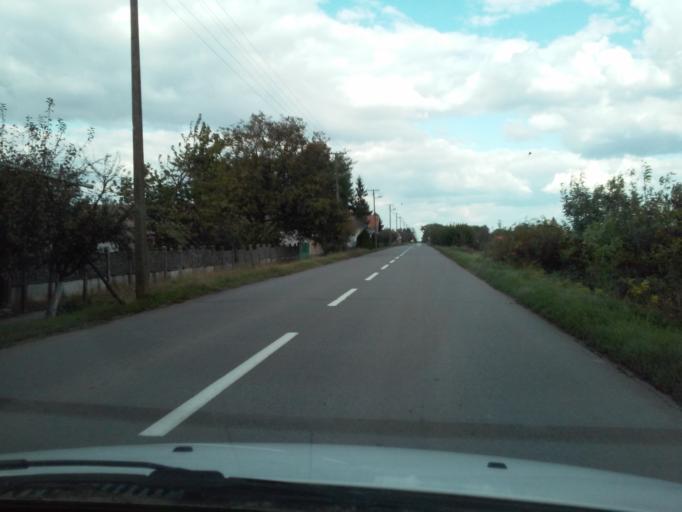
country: RS
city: Sajan
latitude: 45.8438
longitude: 20.2653
